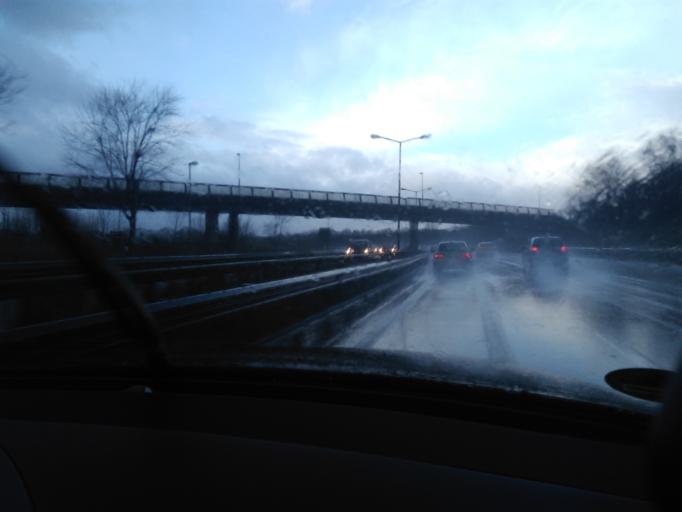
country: DE
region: Hamburg
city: Fuhlsbuettel
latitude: 53.6372
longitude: 10.0096
